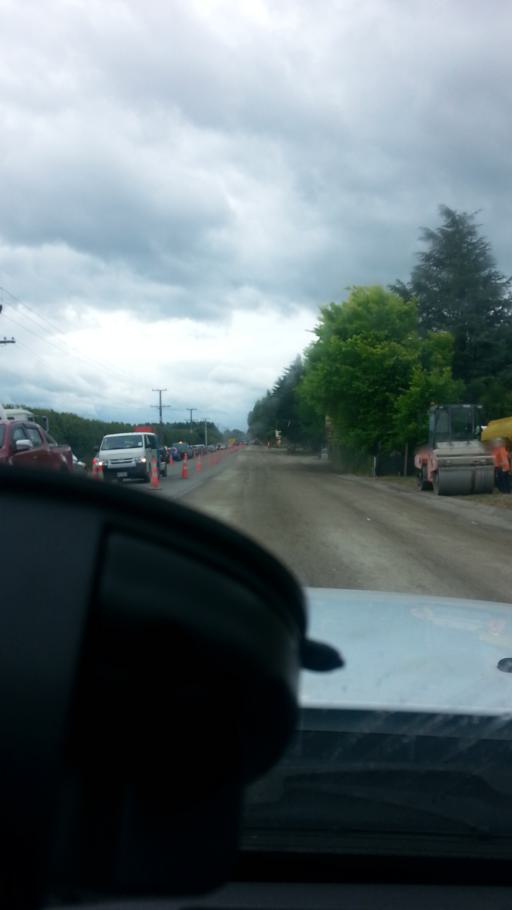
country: NZ
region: Wellington
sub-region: Masterton District
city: Masterton
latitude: -41.0694
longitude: 175.4725
